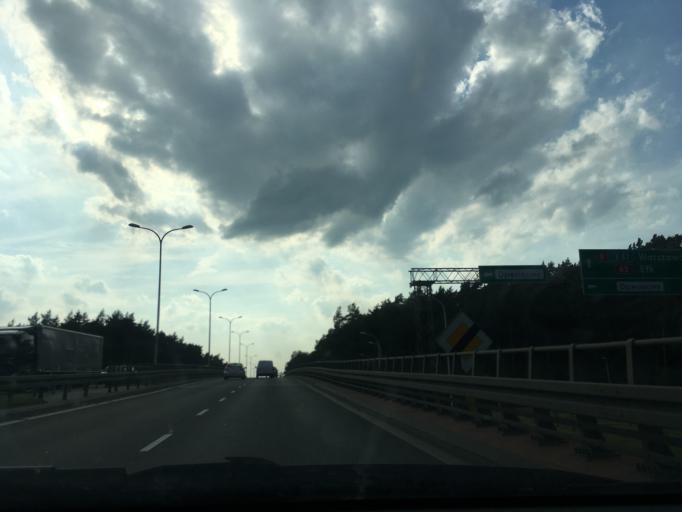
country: PL
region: Podlasie
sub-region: Bialystok
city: Bialystok
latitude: 53.1596
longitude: 23.1433
